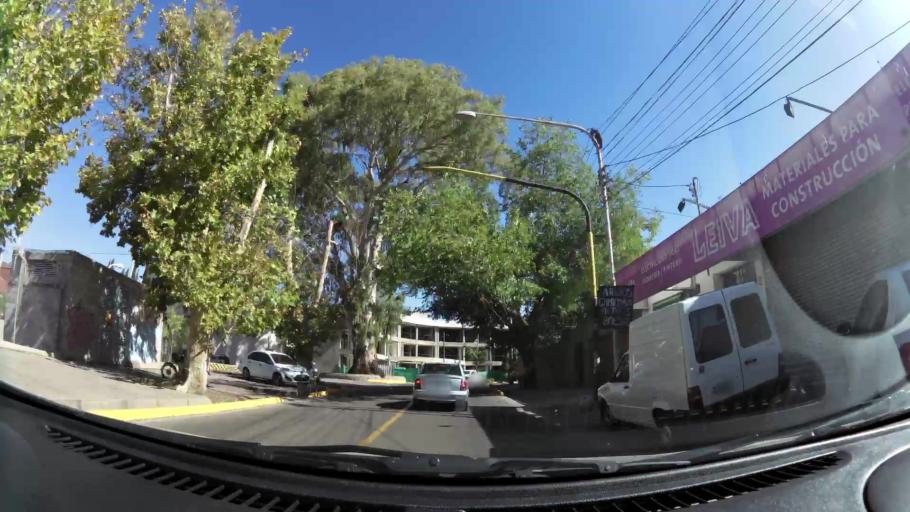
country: AR
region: Mendoza
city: Villa Nueva
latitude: -32.9091
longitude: -68.7909
